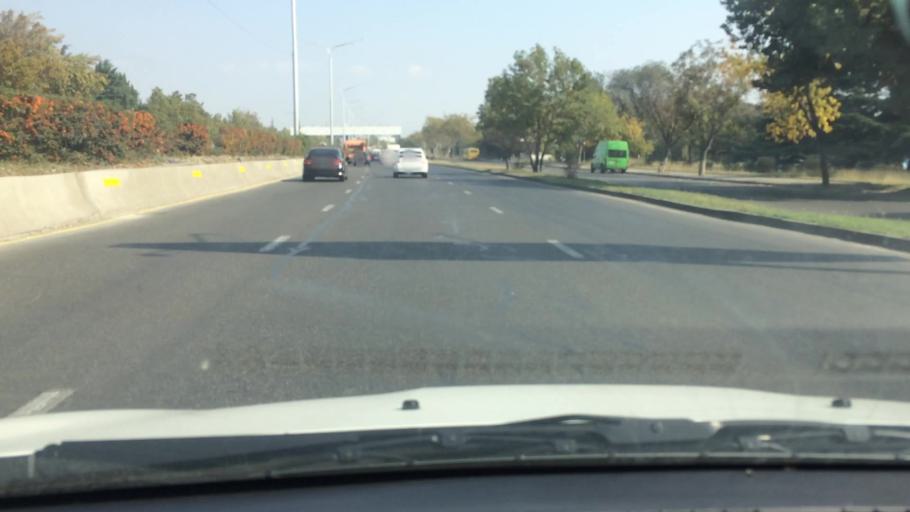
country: GE
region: T'bilisi
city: Tbilisi
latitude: 41.6879
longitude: 44.9005
